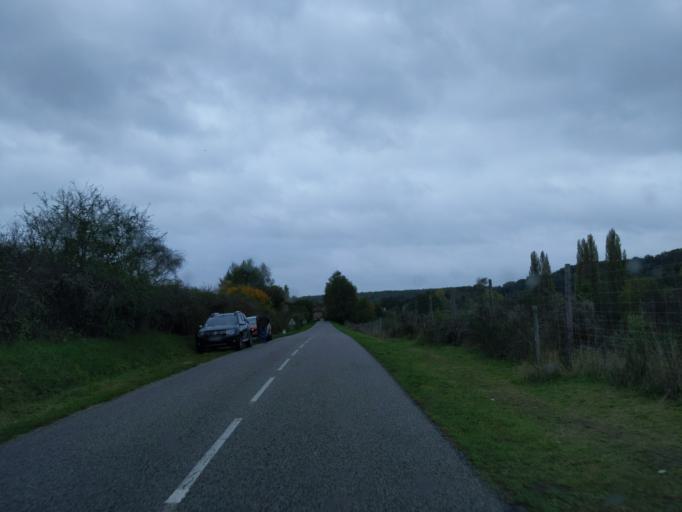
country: FR
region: Ile-de-France
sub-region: Departement des Yvelines
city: Bullion
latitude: 48.6325
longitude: 1.9577
